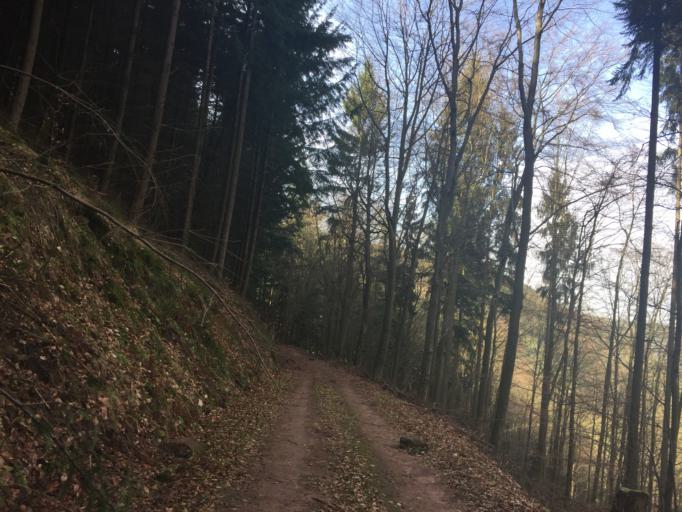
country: DE
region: Rheinland-Pfalz
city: Ramberg
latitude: 49.3109
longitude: 8.0310
